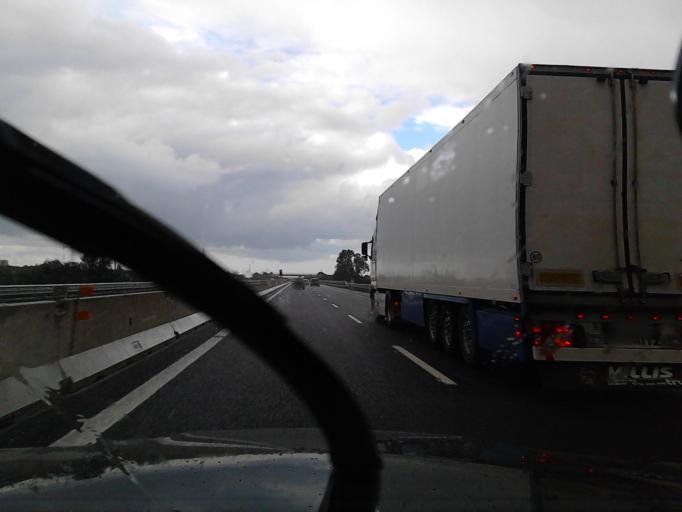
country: IT
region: Apulia
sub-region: Provincia di Bari
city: Molfetta
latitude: 41.1625
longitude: 16.6267
